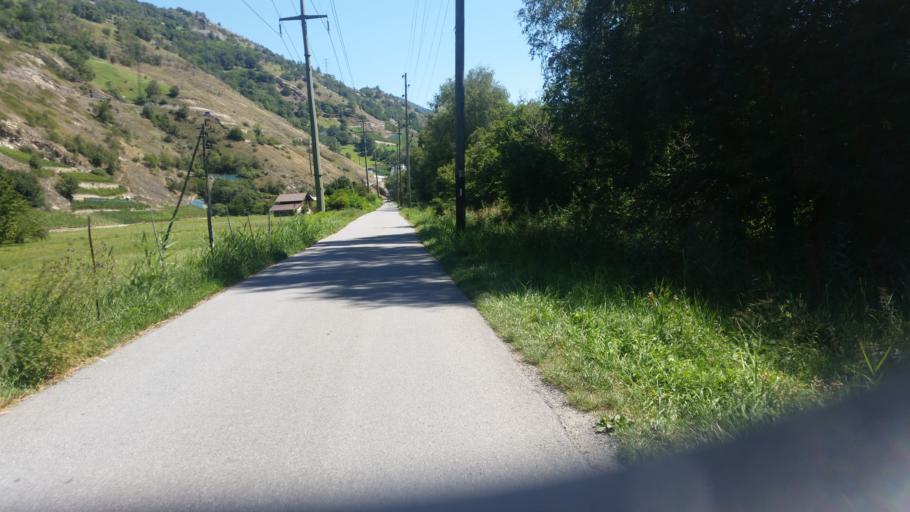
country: CH
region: Valais
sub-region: Raron District
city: Raron
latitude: 46.3083
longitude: 7.8220
